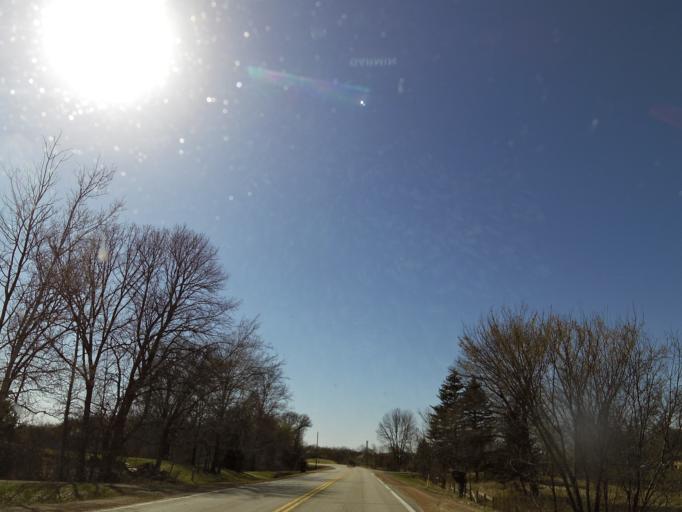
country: US
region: Minnesota
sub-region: Scott County
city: Prior Lake
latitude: 44.6708
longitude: -93.3512
